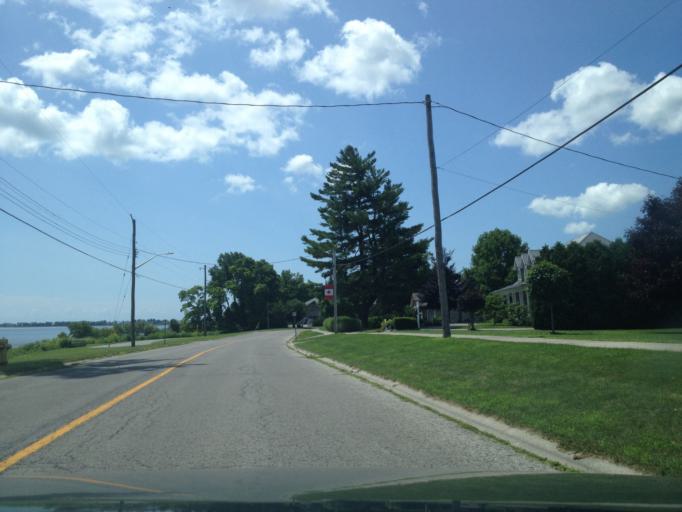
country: CA
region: Ontario
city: Norfolk County
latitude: 42.6297
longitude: -80.4442
